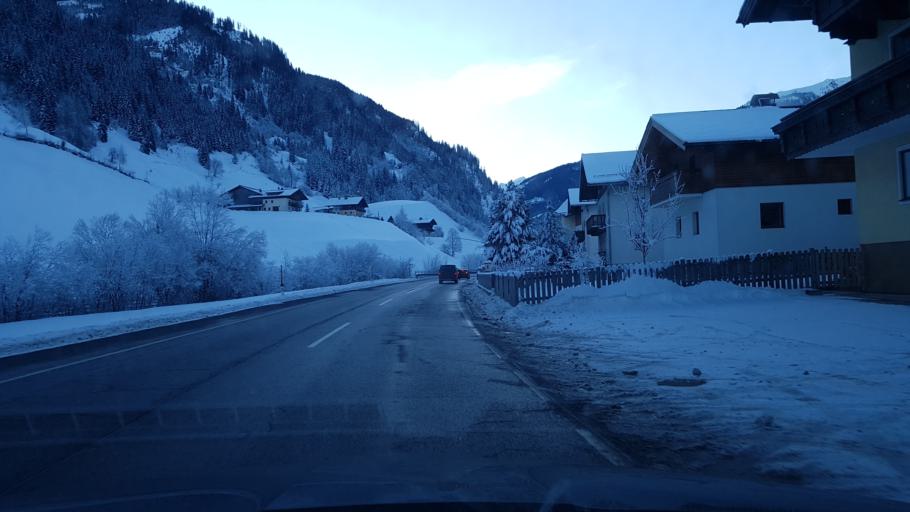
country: AT
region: Salzburg
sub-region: Politischer Bezirk Sankt Johann im Pongau
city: Huttschlag
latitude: 47.2131
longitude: 13.1987
